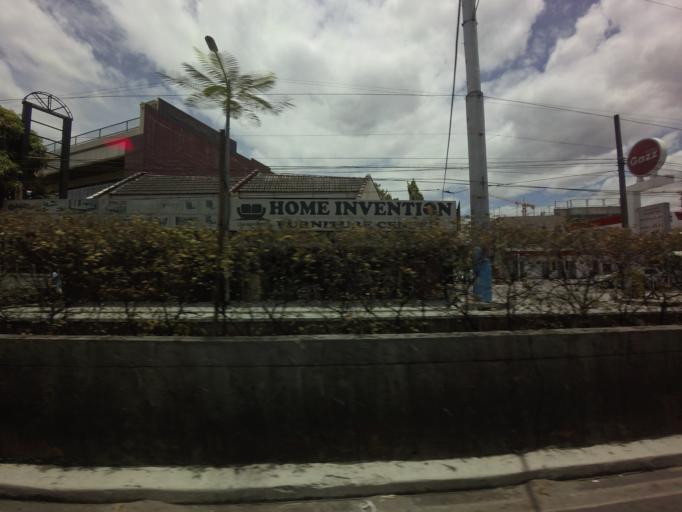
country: PH
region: Metro Manila
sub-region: Marikina
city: Calumpang
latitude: 14.6148
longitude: 121.1022
